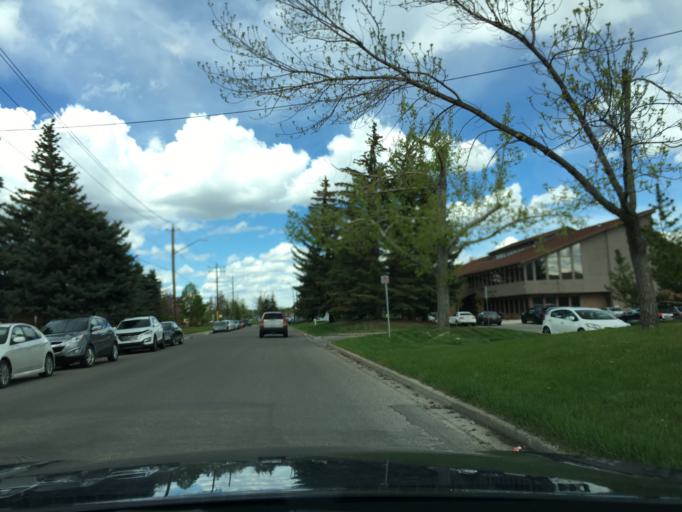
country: CA
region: Alberta
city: Calgary
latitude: 50.9103
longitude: -114.0636
